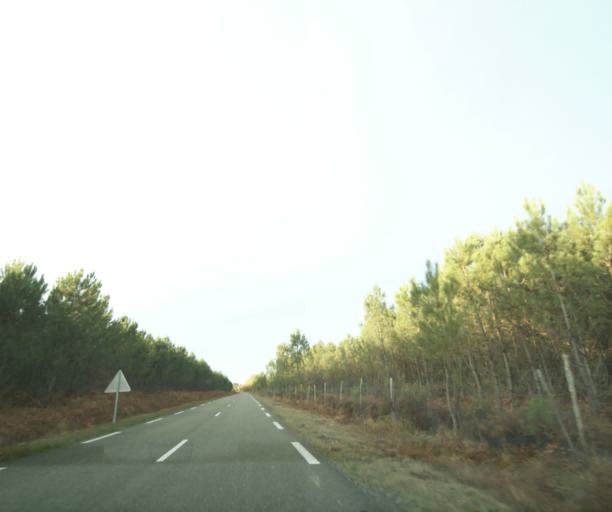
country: FR
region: Aquitaine
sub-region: Departement des Landes
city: Gabarret
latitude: 44.1181
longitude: -0.1056
